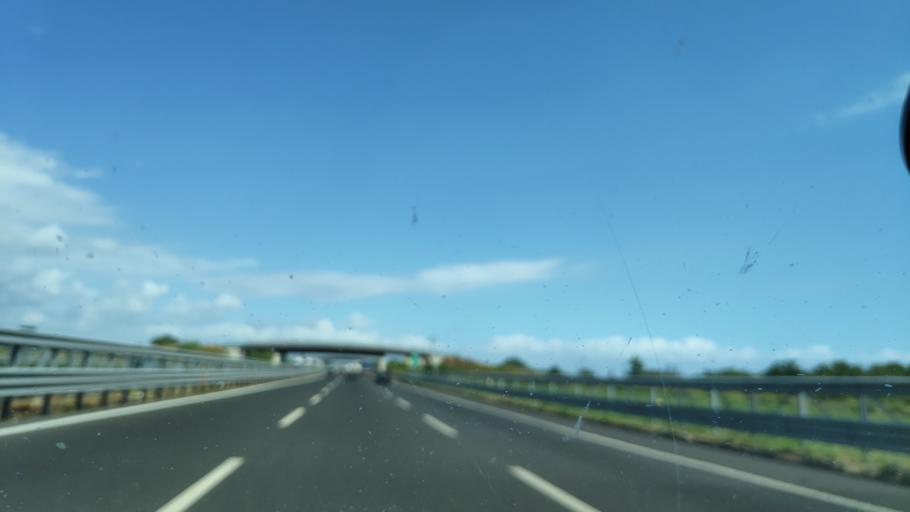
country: IT
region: Campania
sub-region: Provincia di Salerno
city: Pontecagnano
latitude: 40.6511
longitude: 14.8767
